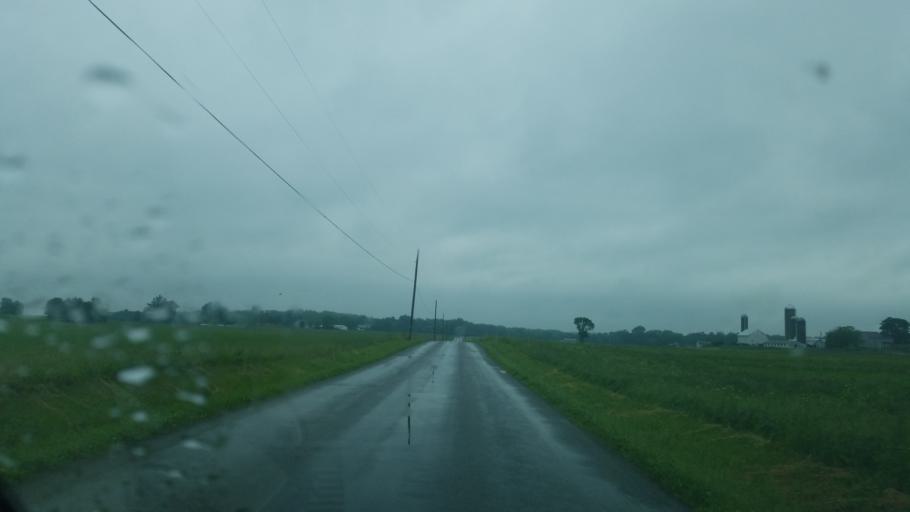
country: US
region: Ohio
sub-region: Huron County
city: Greenwich
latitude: 40.9387
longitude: -82.5365
